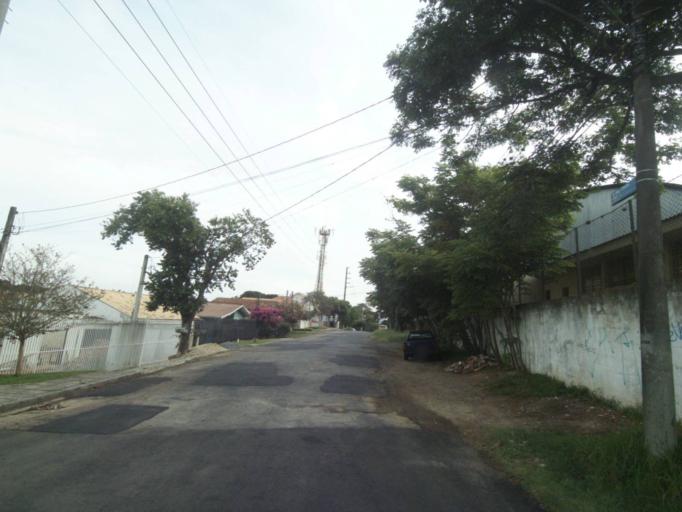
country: BR
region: Parana
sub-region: Curitiba
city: Curitiba
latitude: -25.4114
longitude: -49.2932
